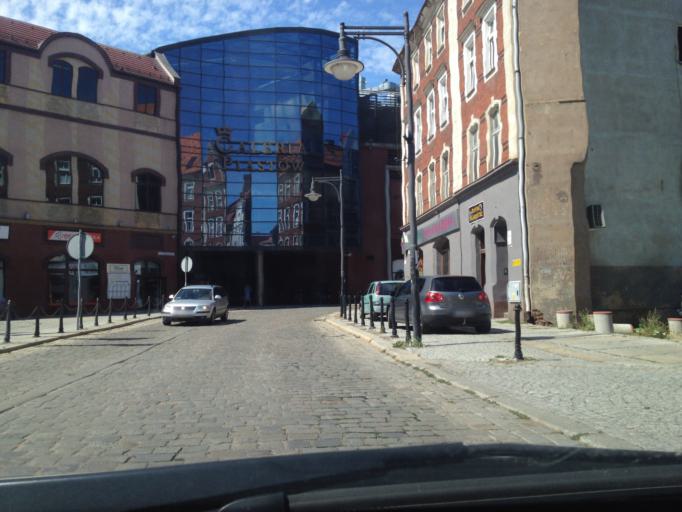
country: PL
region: Lower Silesian Voivodeship
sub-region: Legnica
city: Legnica
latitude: 51.2100
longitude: 16.1652
